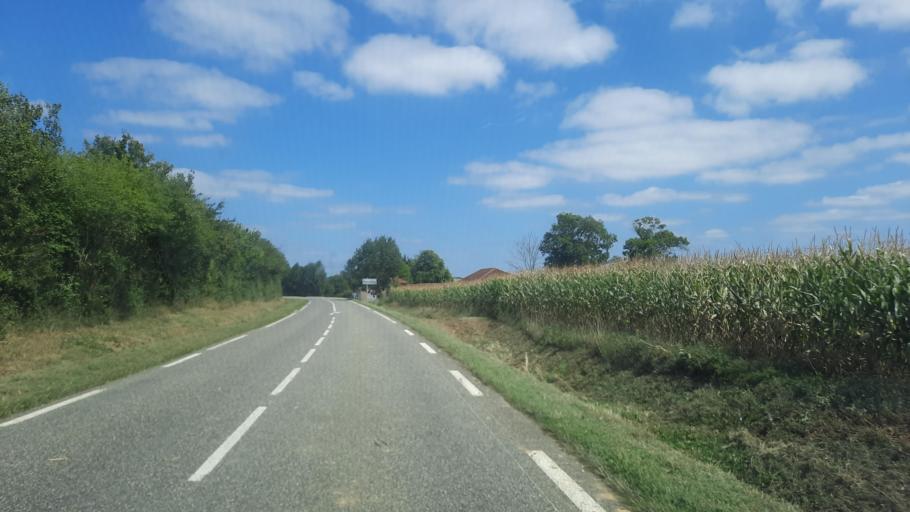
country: FR
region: Midi-Pyrenees
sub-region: Departement du Gers
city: Lombez
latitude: 43.4323
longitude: 0.8419
